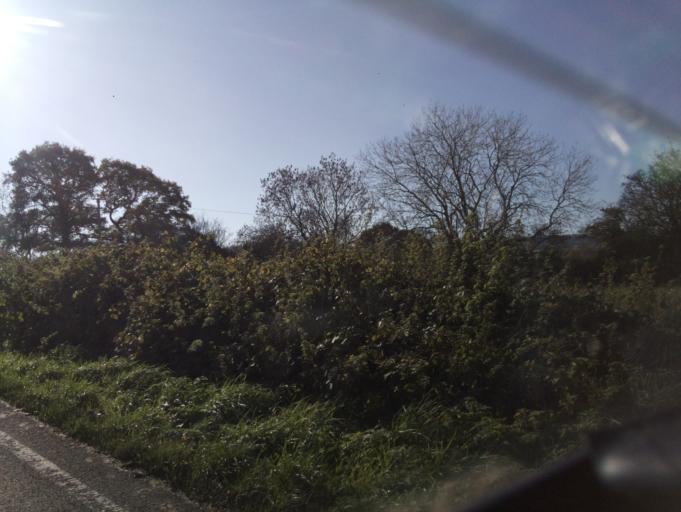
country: GB
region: England
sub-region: Dorset
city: Sherborne
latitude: 50.8584
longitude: -2.4667
